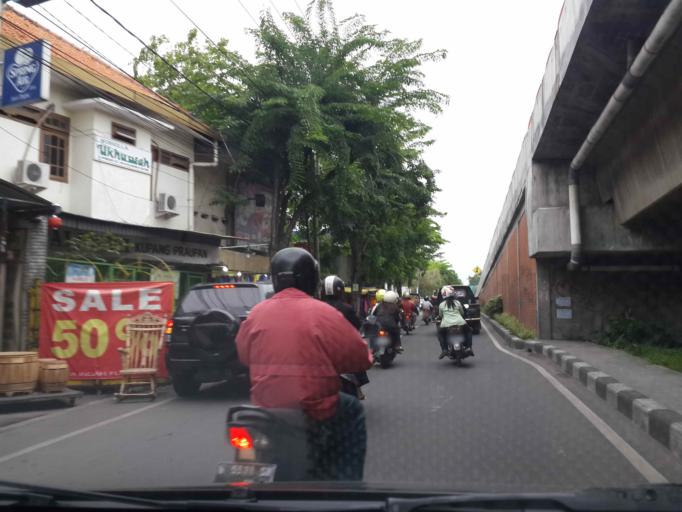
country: ID
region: East Java
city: Gubengairlangga
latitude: -7.2762
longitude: 112.7277
